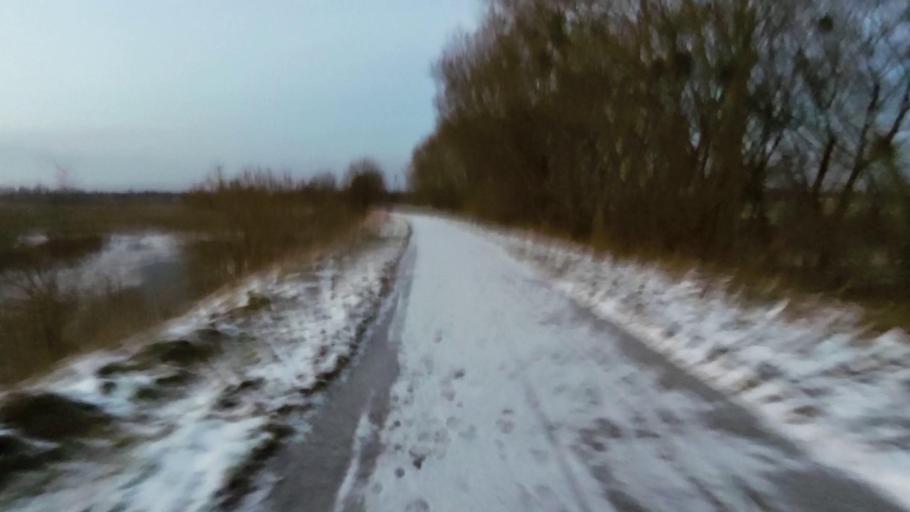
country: PL
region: West Pomeranian Voivodeship
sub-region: Powiat swidwinski
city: Polczyn-Zdroj
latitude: 53.7624
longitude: 16.0686
